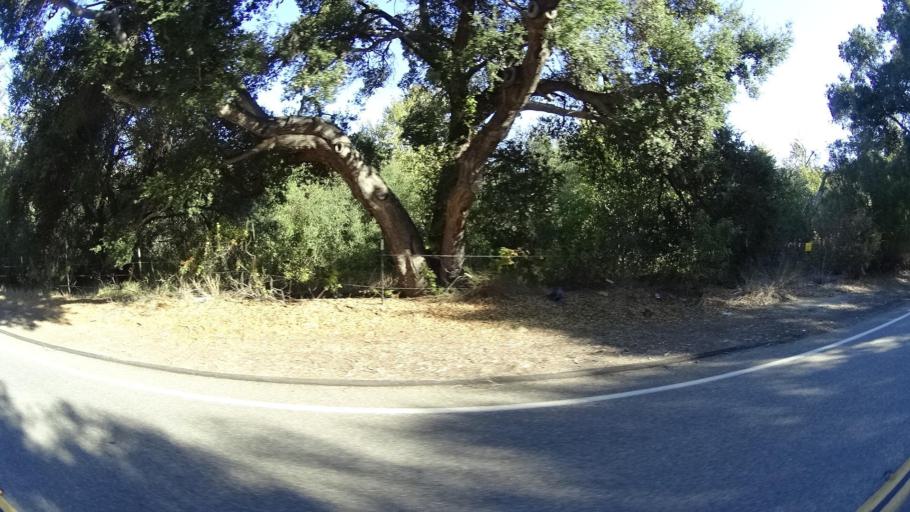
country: US
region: California
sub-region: San Diego County
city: Jamul
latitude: 32.6499
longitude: -116.8640
